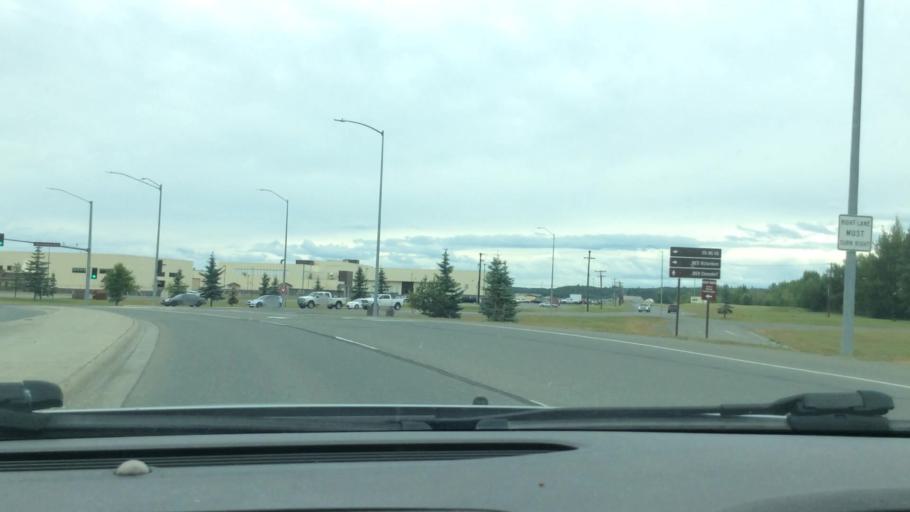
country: US
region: Alaska
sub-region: Anchorage Municipality
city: Anchorage
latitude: 61.2397
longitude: -149.7787
